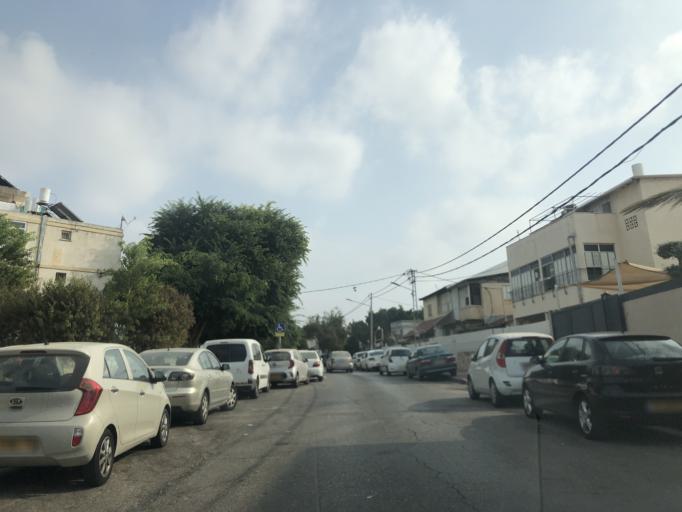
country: IL
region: Central District
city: Rosh Ha'Ayin
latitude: 32.0955
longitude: 34.9508
